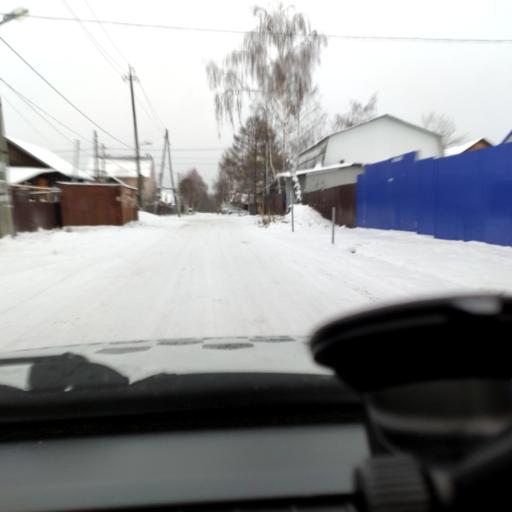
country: RU
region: Perm
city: Perm
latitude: 58.0605
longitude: 56.3650
